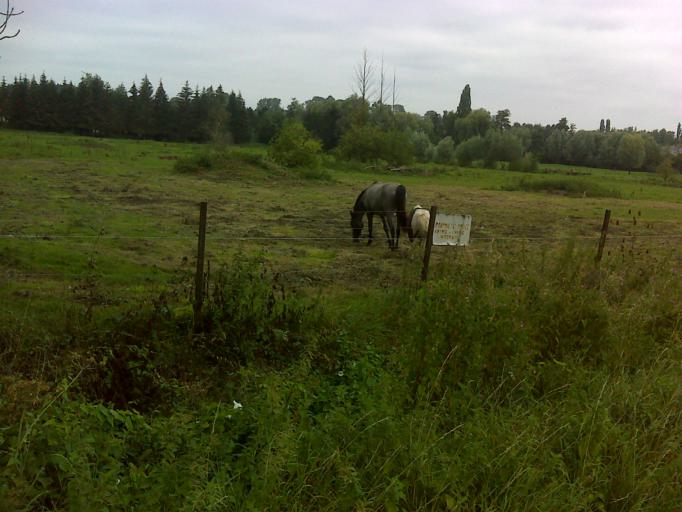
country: FR
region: Nord-Pas-de-Calais
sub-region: Departement du Nord
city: Landrecies
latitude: 50.1243
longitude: 3.6840
